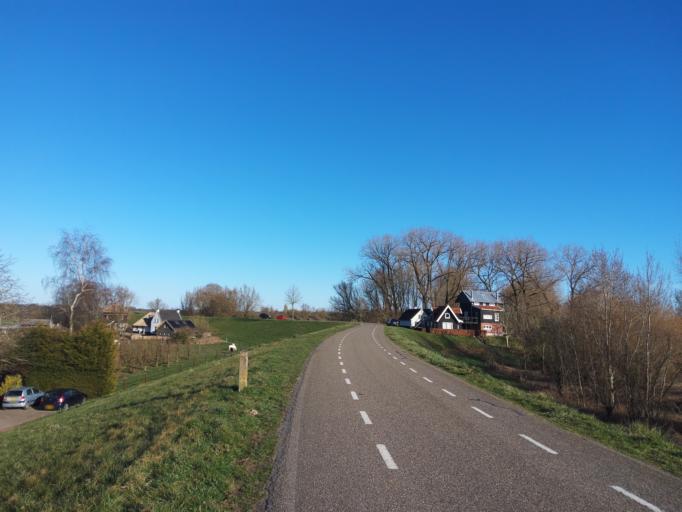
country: NL
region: Gelderland
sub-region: Gemeente Neerijnen
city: Neerijnen
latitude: 51.8283
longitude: 5.3156
